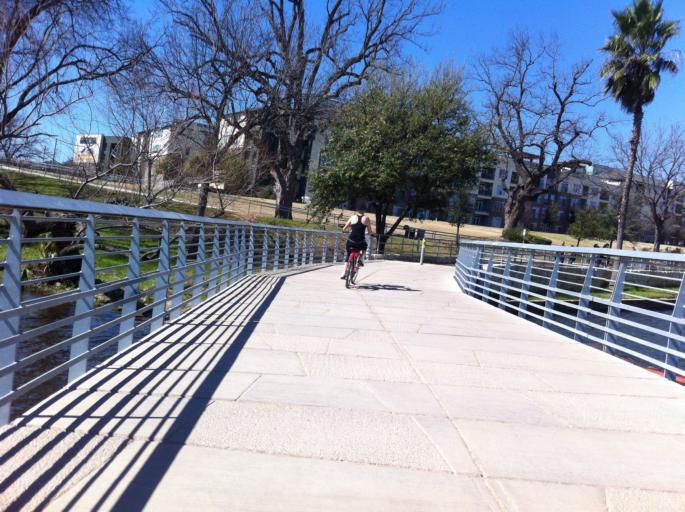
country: US
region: Texas
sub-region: Travis County
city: Austin
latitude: 30.2454
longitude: -97.7257
